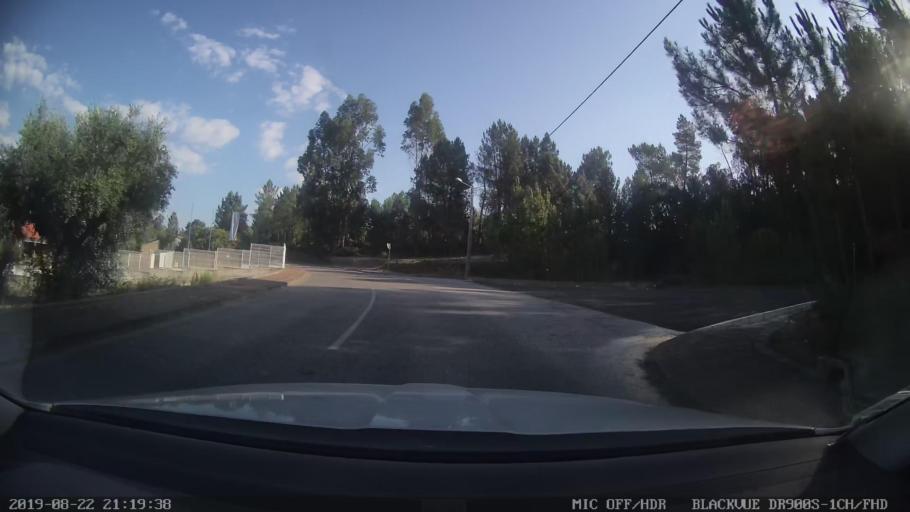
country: PT
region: Castelo Branco
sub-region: Serta
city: Serta
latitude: 39.8071
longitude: -8.1078
